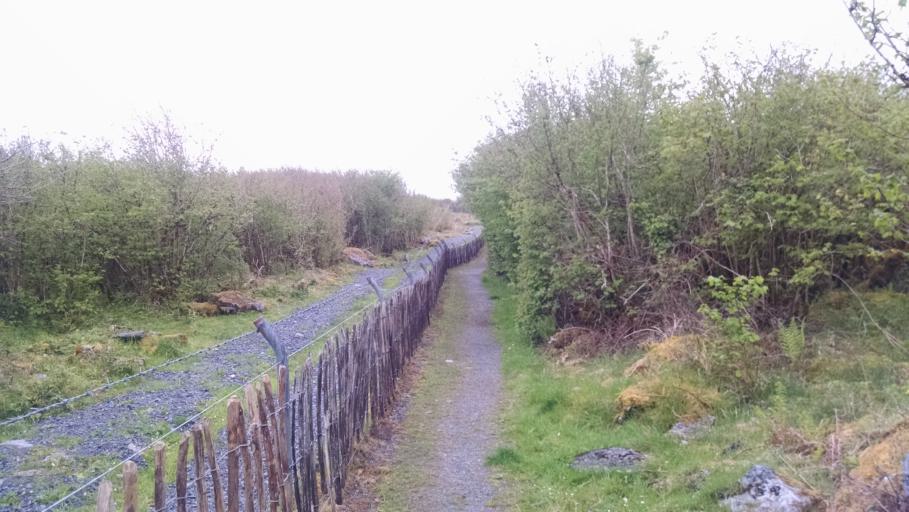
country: IE
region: Munster
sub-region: An Clar
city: Ennis
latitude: 53.0108
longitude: -9.0764
